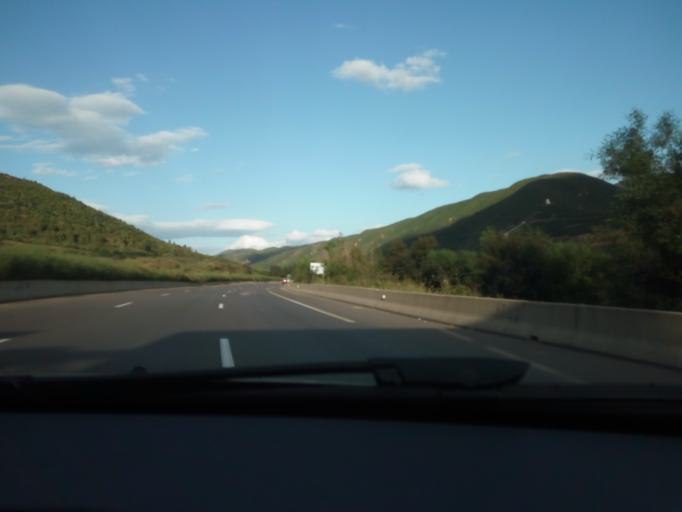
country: DZ
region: Tipaza
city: El Affroun
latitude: 36.3925
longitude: 2.5074
